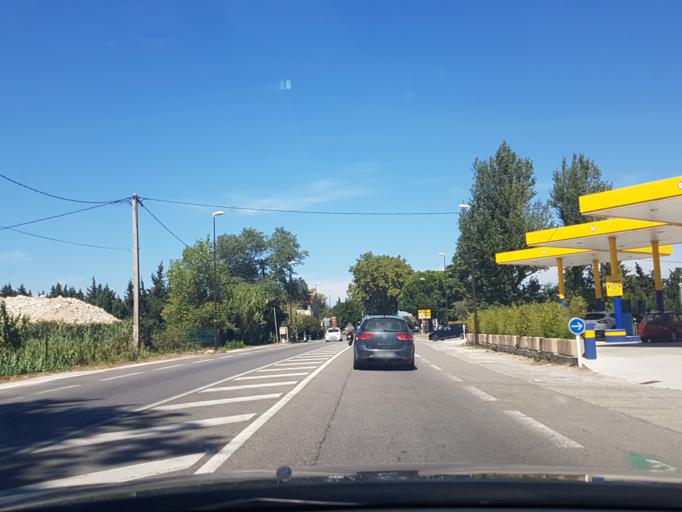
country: FR
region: Provence-Alpes-Cote d'Azur
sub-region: Departement des Bouches-du-Rhone
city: Rognonas
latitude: 43.9187
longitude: 4.8093
